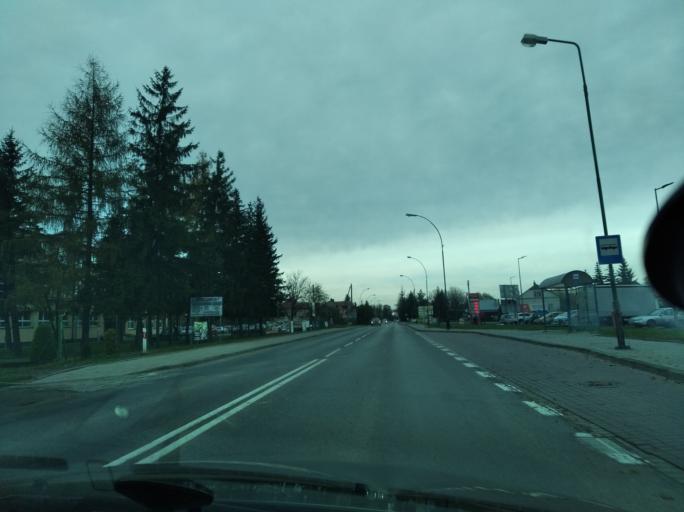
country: PL
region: Subcarpathian Voivodeship
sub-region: Powiat lancucki
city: Lancut
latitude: 50.0909
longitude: 22.2317
